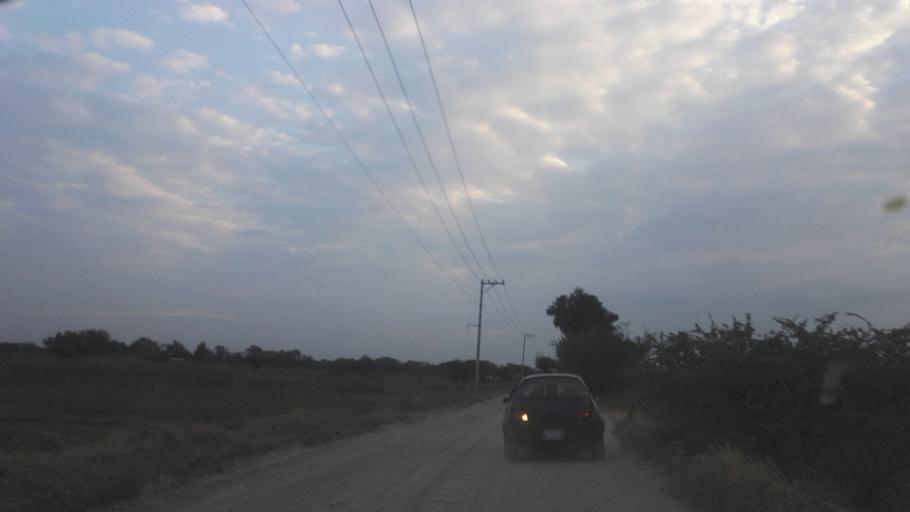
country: MX
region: Guanajuato
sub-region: Leon
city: Ladrilleras del Refugio
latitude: 21.0804
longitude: -101.5570
